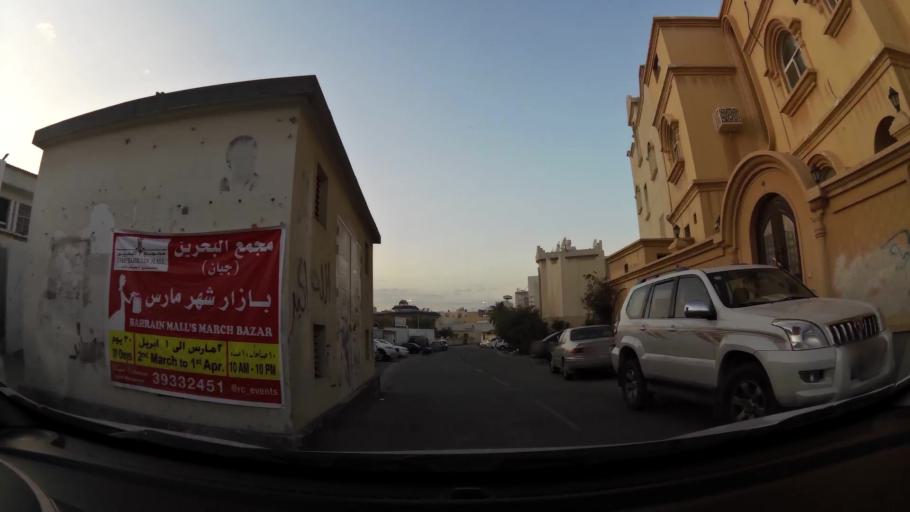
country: BH
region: Manama
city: Jidd Hafs
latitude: 26.2261
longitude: 50.5357
